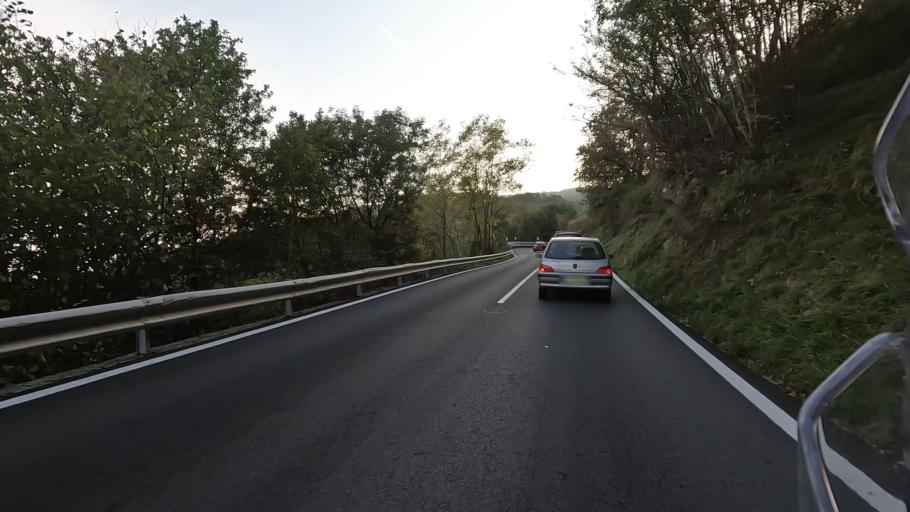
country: IT
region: Liguria
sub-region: Provincia di Savona
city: Osteria dei Cacciatori-Stella
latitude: 44.4203
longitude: 8.4792
